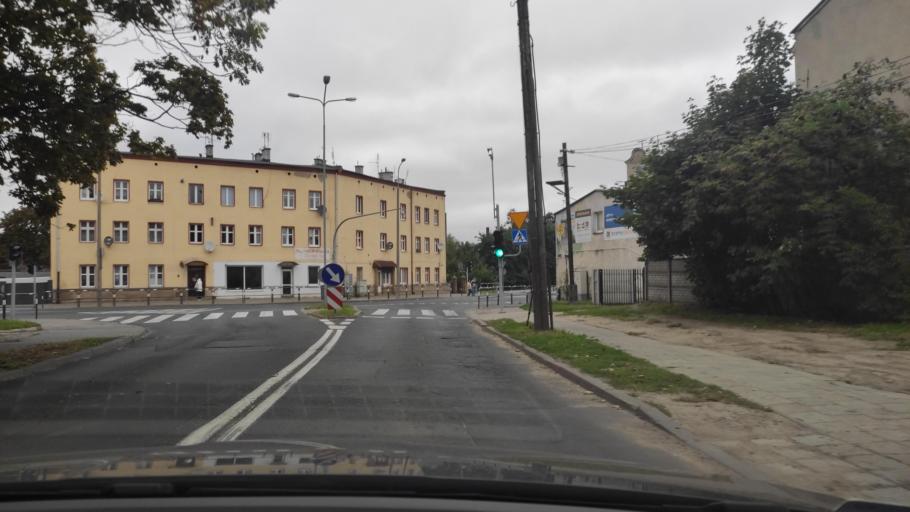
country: PL
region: Greater Poland Voivodeship
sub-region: Powiat poznanski
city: Czerwonak
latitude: 52.4217
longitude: 16.9759
